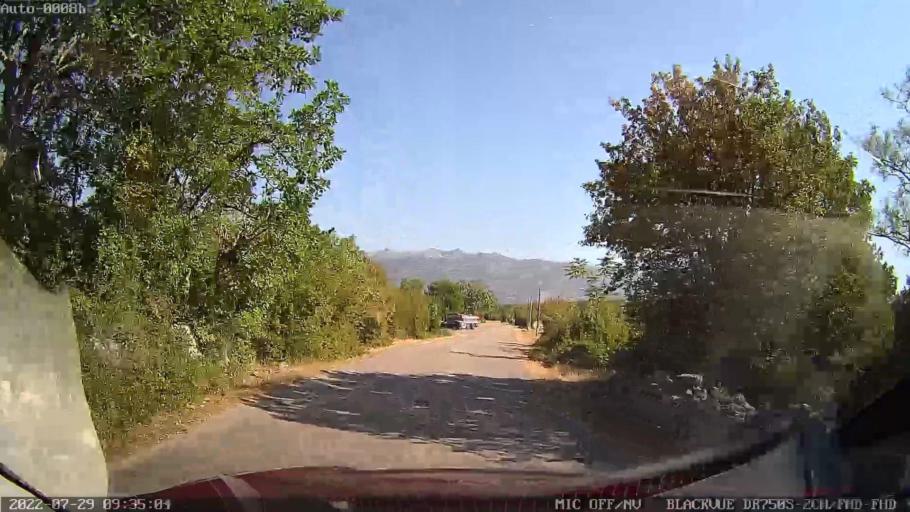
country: HR
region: Zadarska
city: Obrovac
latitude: 44.1832
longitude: 15.7319
